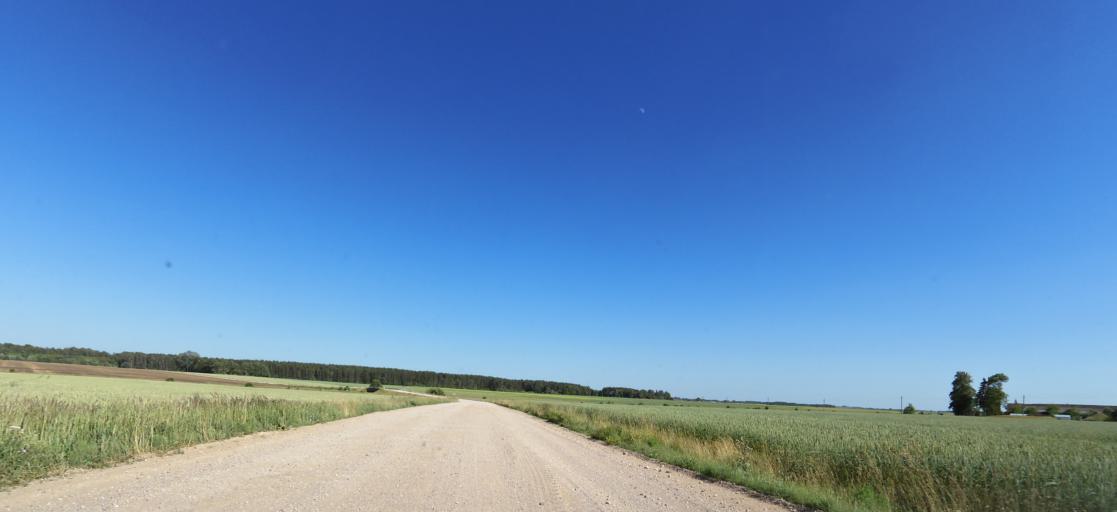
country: LT
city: Vabalninkas
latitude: 56.0226
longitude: 24.6965
